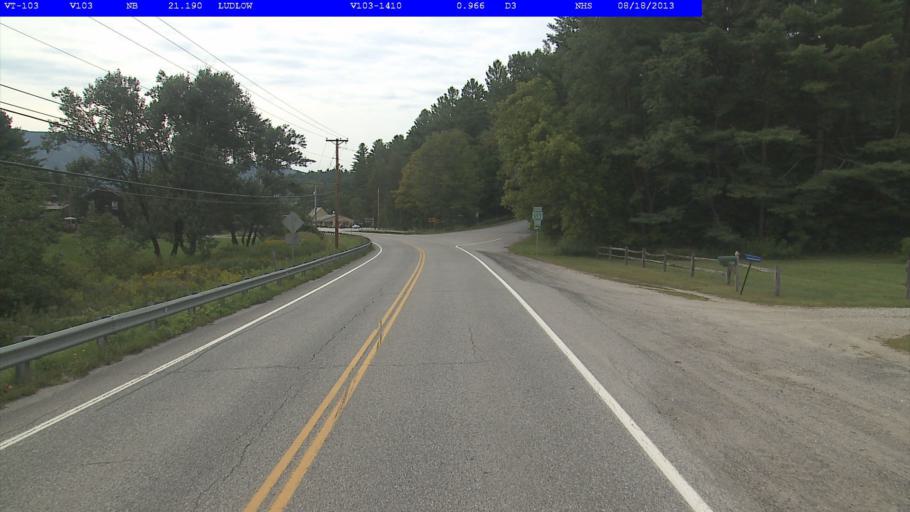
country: US
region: Vermont
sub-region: Windsor County
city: Chester
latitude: 43.3932
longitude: -72.6788
